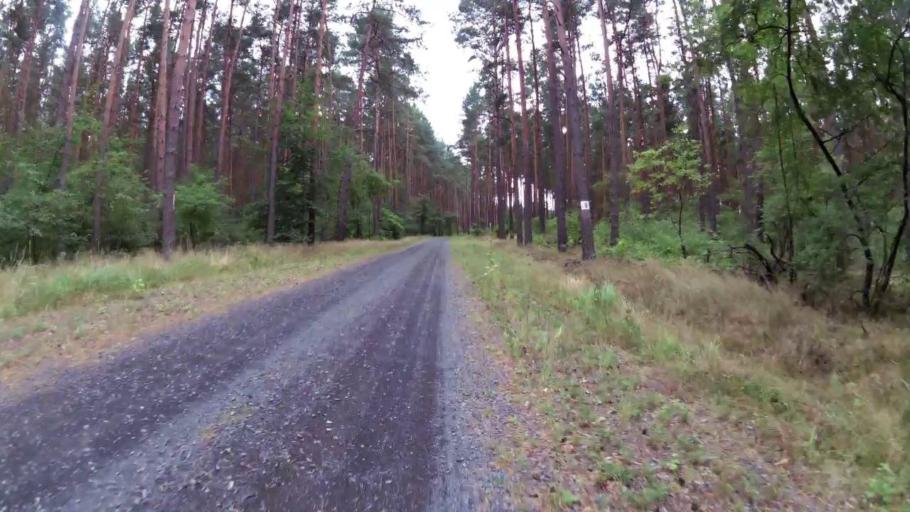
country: PL
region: West Pomeranian Voivodeship
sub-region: Powiat mysliborski
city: Debno
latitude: 52.7761
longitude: 14.7204
